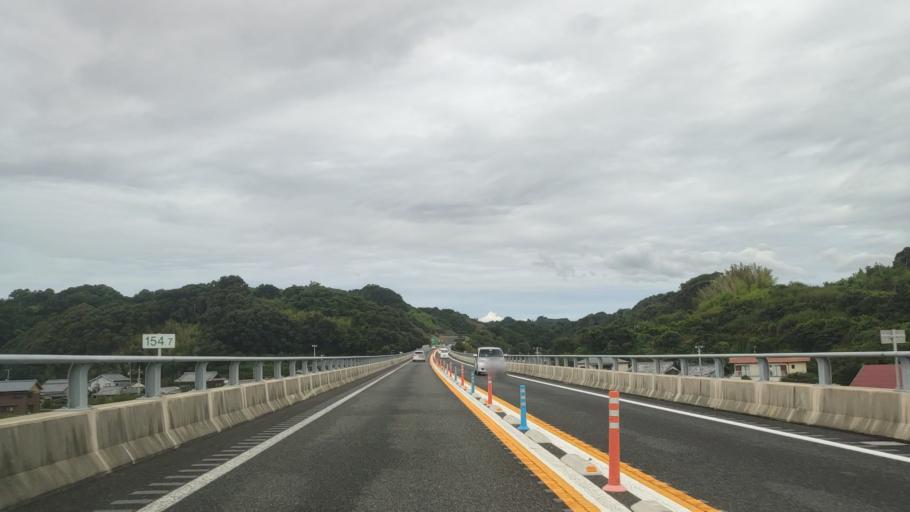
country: JP
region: Wakayama
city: Tanabe
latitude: 33.7542
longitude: 135.3568
